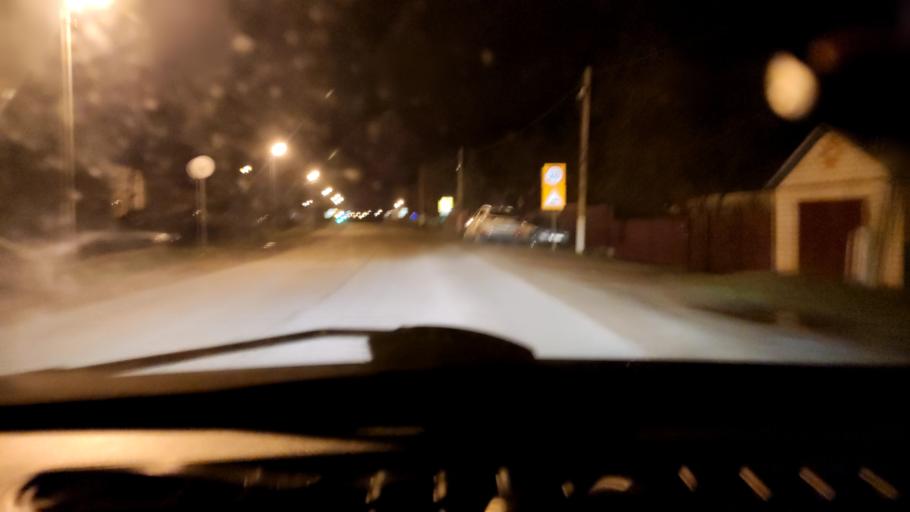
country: RU
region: Bashkortostan
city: Karmaskaly
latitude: 54.3660
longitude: 56.1721
